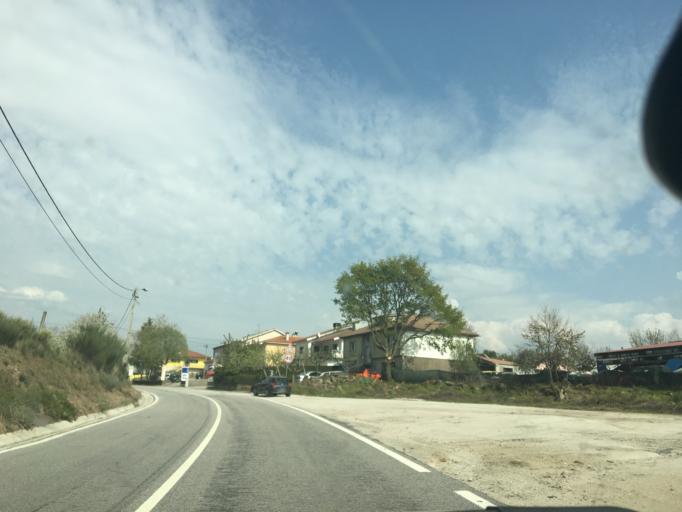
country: PT
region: Vila Real
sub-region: Boticas
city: Boticas
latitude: 41.6804
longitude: -7.7054
